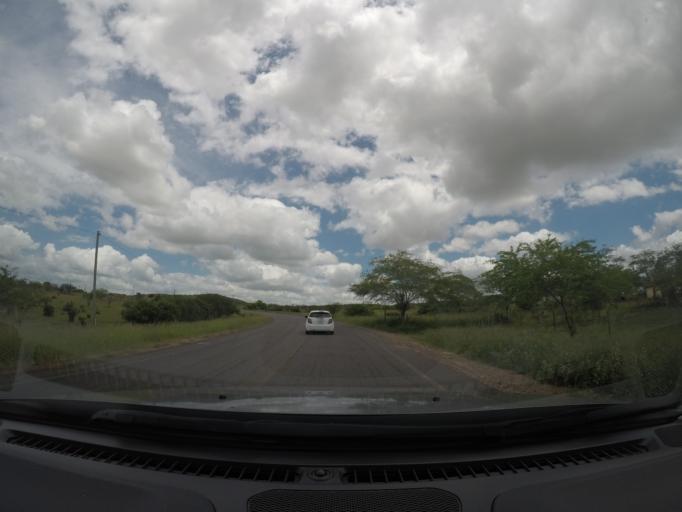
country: BR
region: Bahia
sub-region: Ipira
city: Ipira
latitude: -12.2719
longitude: -39.8401
